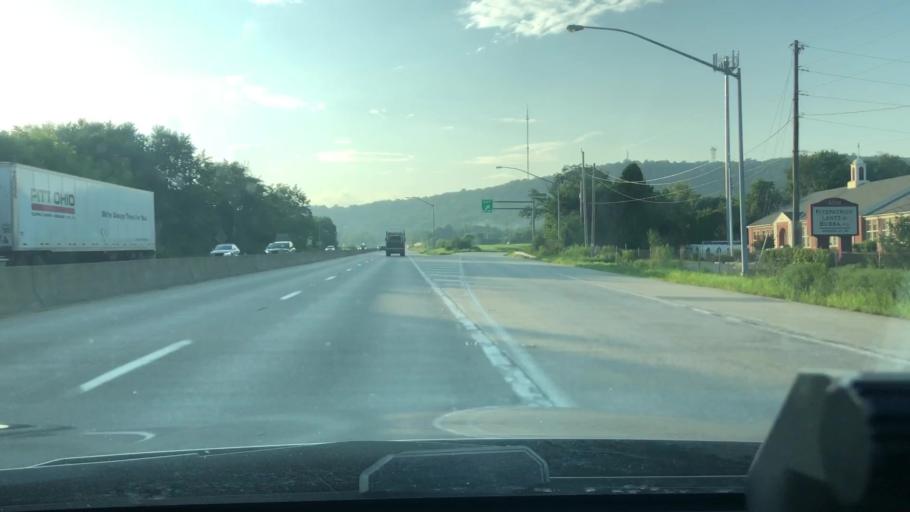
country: US
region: Pennsylvania
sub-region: Lehigh County
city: Coopersburg
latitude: 40.5509
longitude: -75.4272
